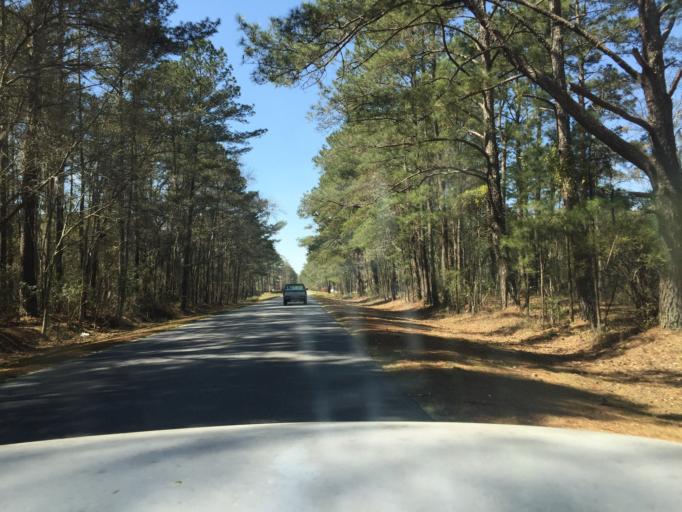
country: US
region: Georgia
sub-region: Chatham County
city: Bloomingdale
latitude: 32.0950
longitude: -81.3273
